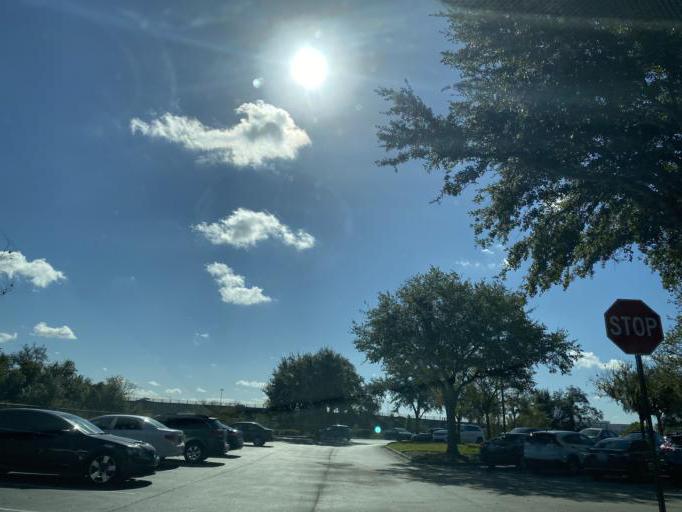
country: US
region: Florida
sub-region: Seminole County
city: Heathrow
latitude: 28.7880
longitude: -81.3518
